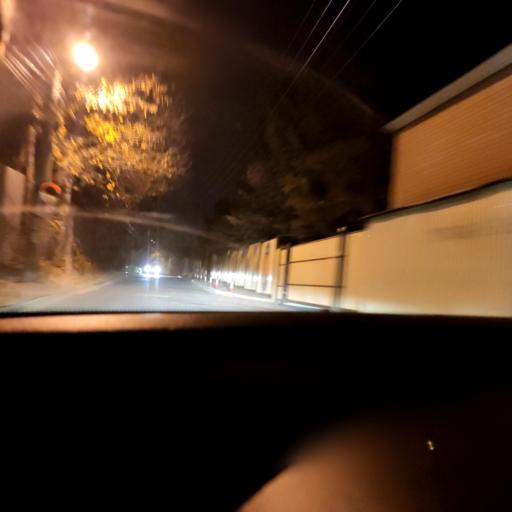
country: RU
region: Samara
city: Samara
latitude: 53.2685
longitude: 50.1902
